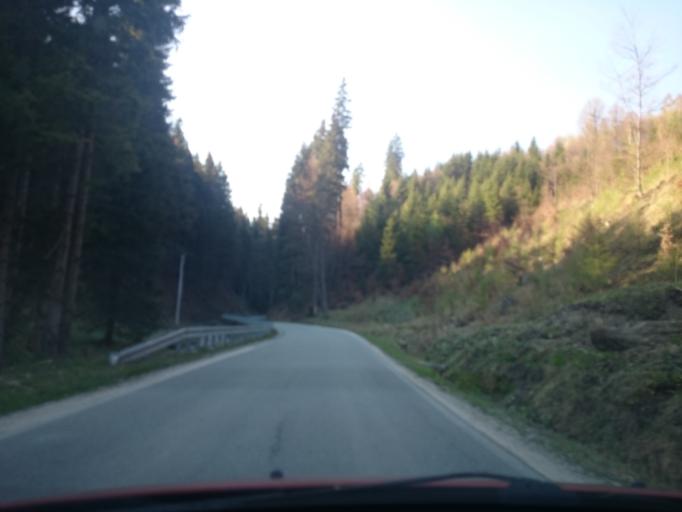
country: PL
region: Lower Silesian Voivodeship
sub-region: Powiat klodzki
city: Duszniki-Zdroj
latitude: 50.3634
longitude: 16.3930
